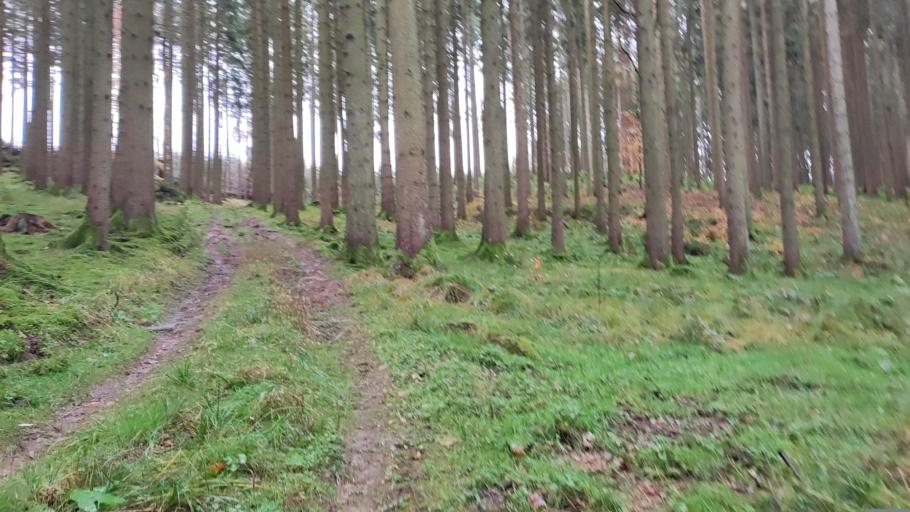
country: DE
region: Bavaria
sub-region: Swabia
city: Dinkelscherben
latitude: 48.3563
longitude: 10.5255
